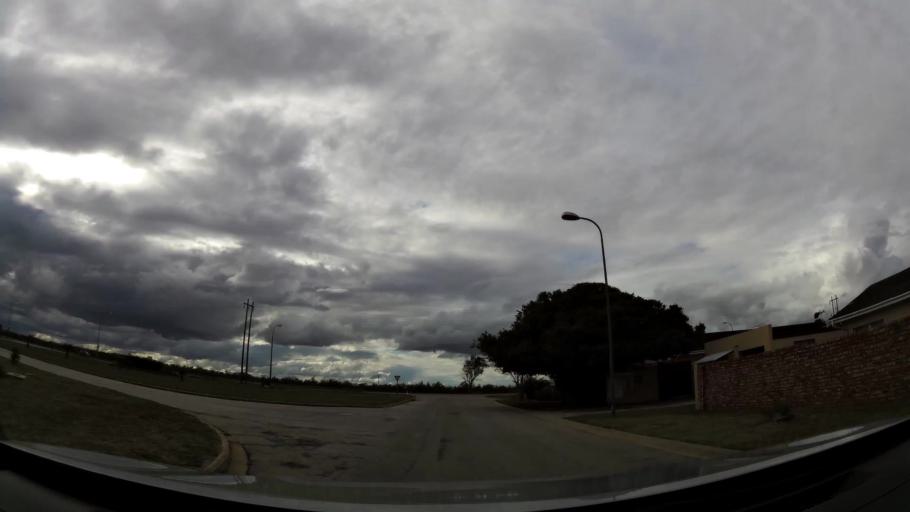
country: ZA
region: Eastern Cape
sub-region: Nelson Mandela Bay Metropolitan Municipality
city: Port Elizabeth
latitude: -33.9363
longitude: 25.4739
